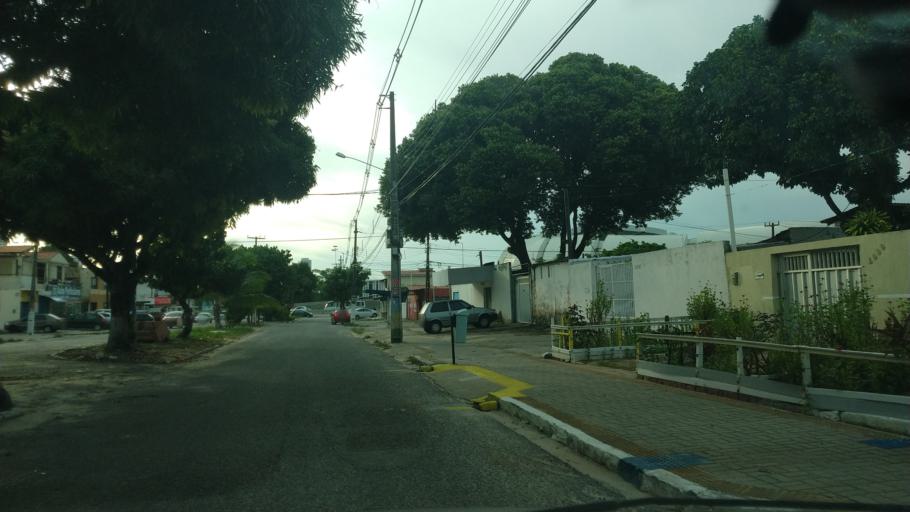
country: BR
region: Rio Grande do Norte
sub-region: Natal
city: Natal
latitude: -5.8299
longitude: -35.2099
